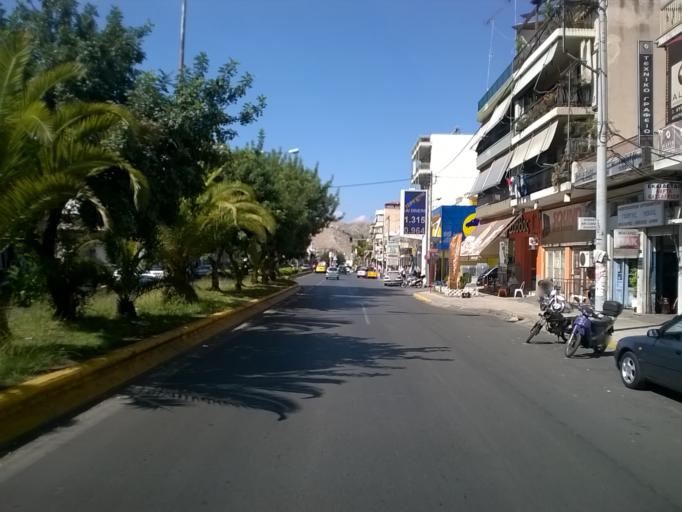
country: GR
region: Attica
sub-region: Nomos Piraios
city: Keratsini
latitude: 37.9641
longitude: 23.6279
